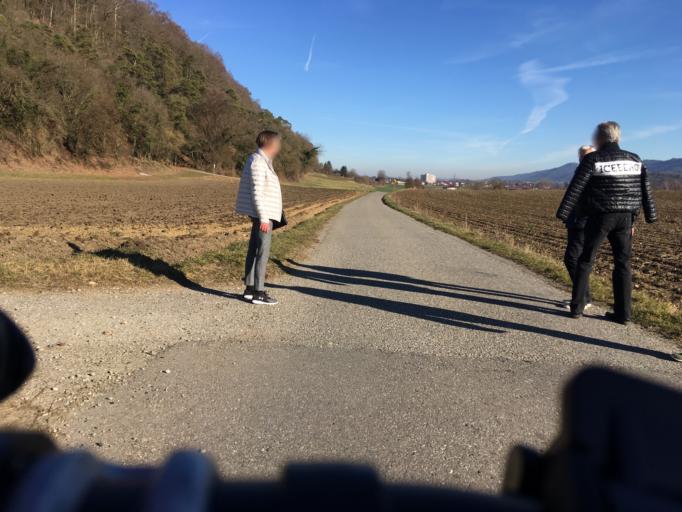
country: CH
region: Schaffhausen
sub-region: Bezirk Stein
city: Ramsen
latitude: 47.7314
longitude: 8.8084
